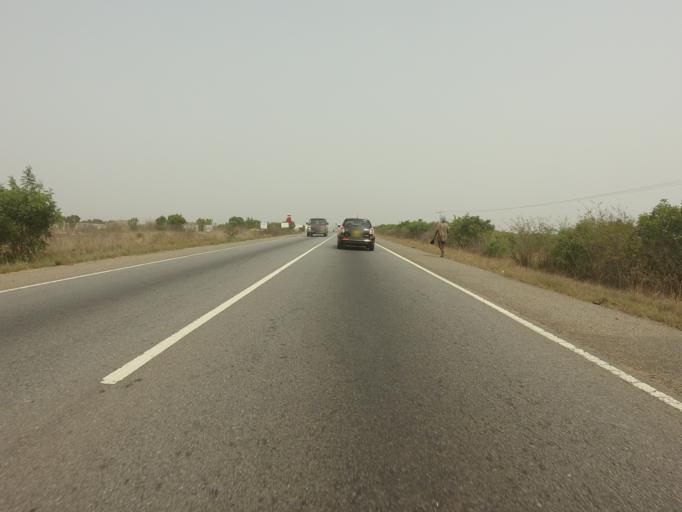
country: GH
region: Greater Accra
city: Tema
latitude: 5.8587
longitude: 0.2731
